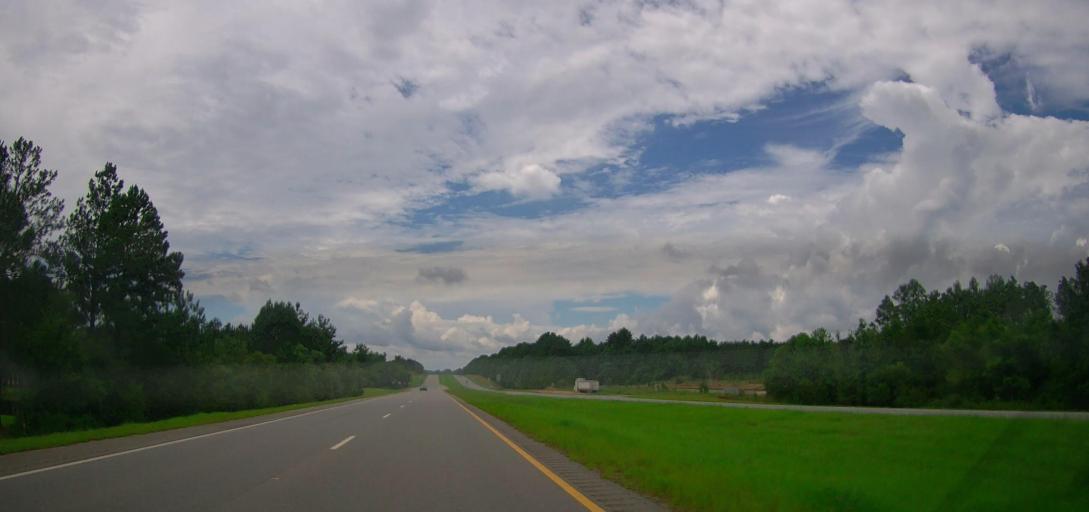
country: US
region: Georgia
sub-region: Telfair County
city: Helena
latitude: 32.0905
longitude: -82.9398
